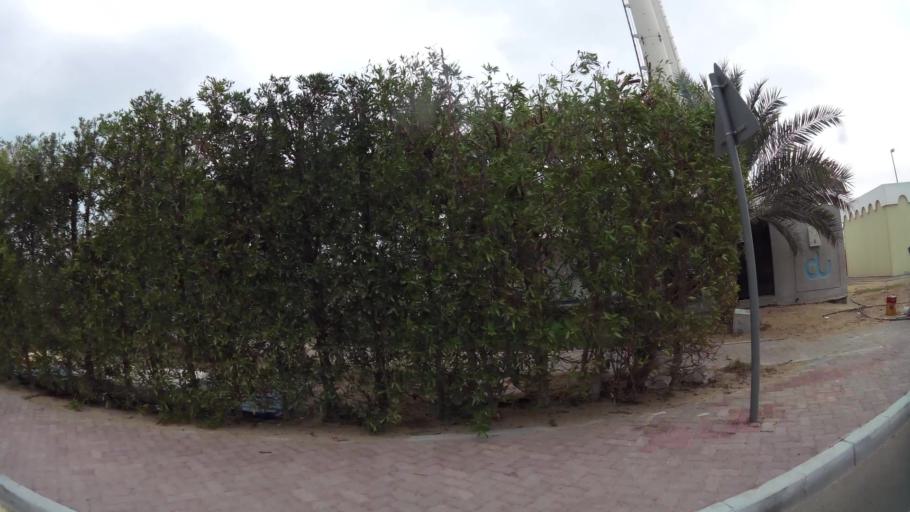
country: AE
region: Abu Dhabi
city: Abu Dhabi
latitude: 24.4359
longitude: 54.3853
